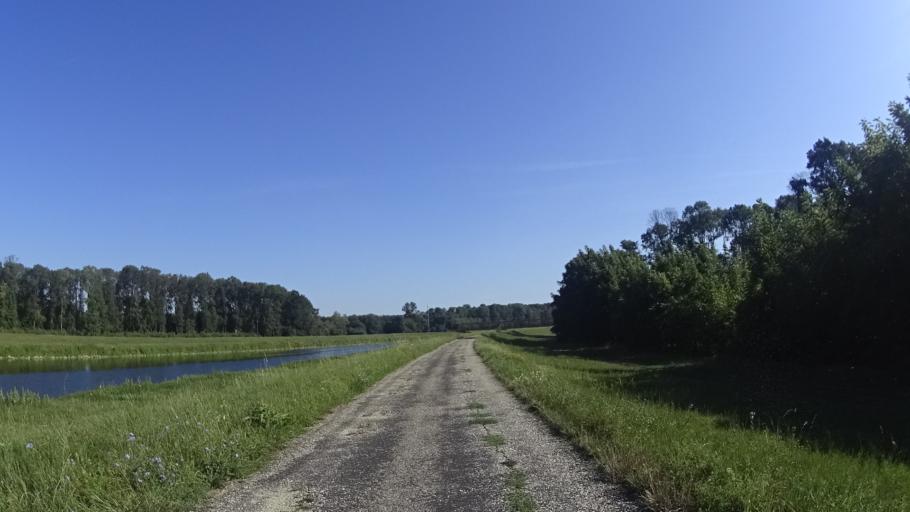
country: CZ
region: South Moravian
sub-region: Okres Breclav
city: Lanzhot
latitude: 48.7072
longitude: 16.9978
